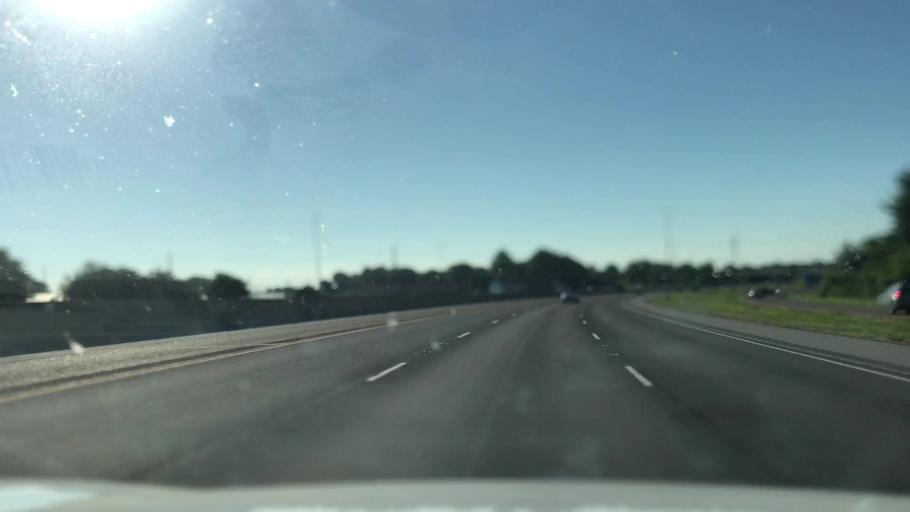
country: US
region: Illinois
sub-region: Saint Clair County
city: O'Fallon
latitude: 38.5956
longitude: -89.9504
